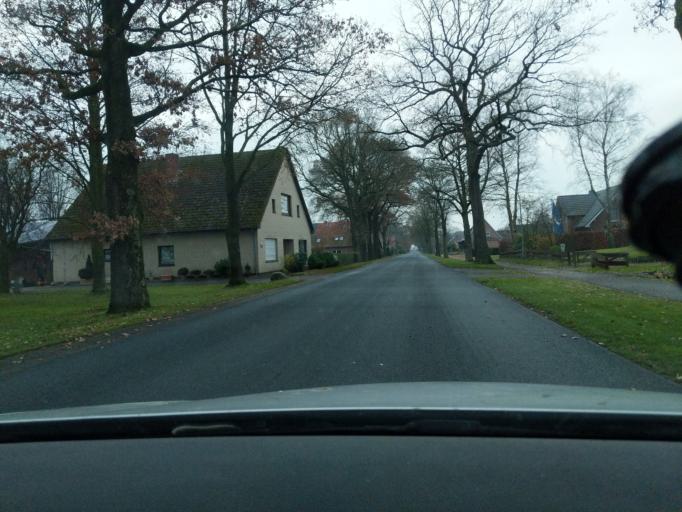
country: DE
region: Lower Saxony
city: Ahlerstedt
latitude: 53.3997
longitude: 9.4910
